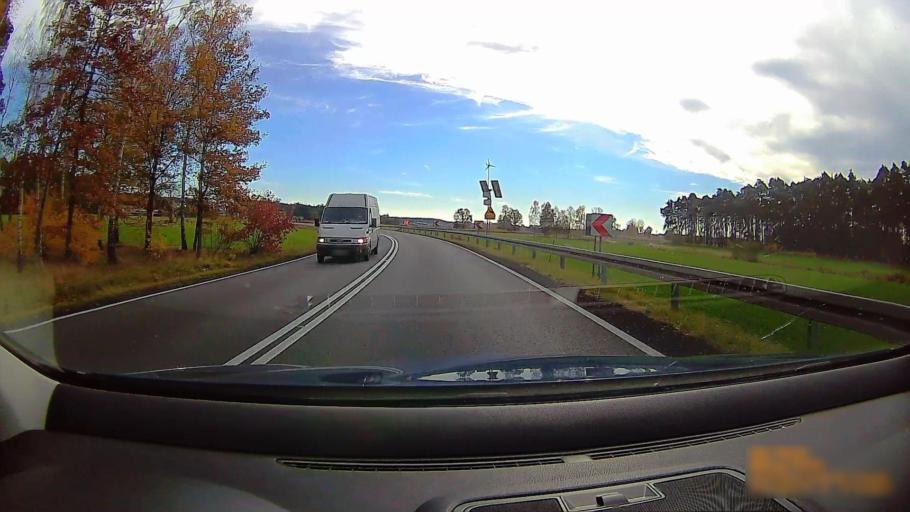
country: PL
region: Greater Poland Voivodeship
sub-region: Powiat ostrzeszowski
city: Ostrzeszow
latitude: 51.4908
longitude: 17.8575
